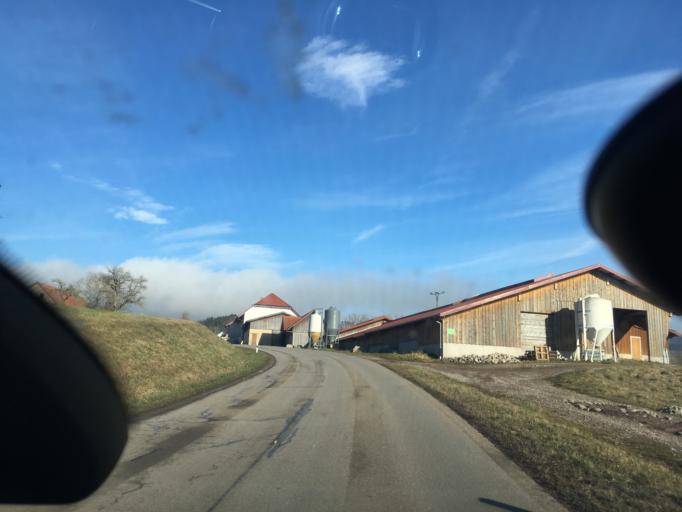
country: DE
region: Baden-Wuerttemberg
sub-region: Freiburg Region
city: Dogern
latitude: 47.6546
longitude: 8.1466
